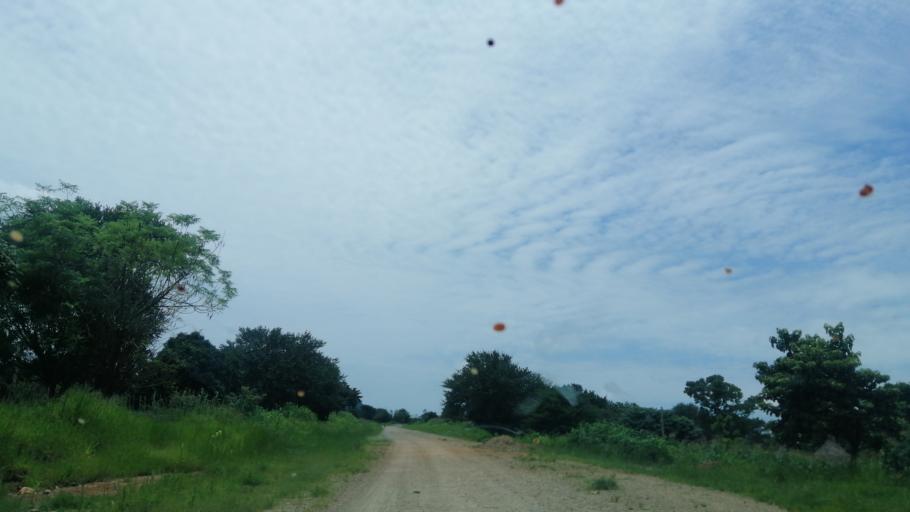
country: ET
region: Oromiya
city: Mendi
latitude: 10.1671
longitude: 35.0938
